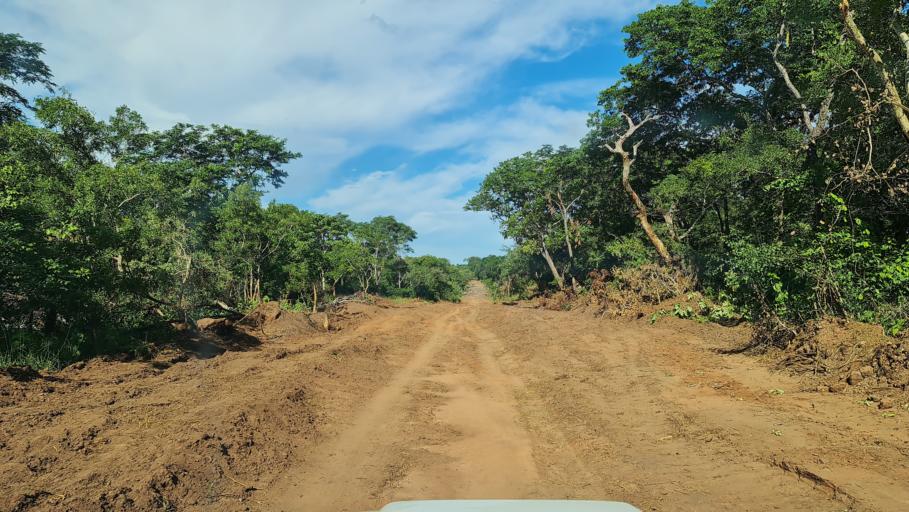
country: MZ
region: Nampula
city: Antonio Enes
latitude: -15.5086
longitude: 40.1387
